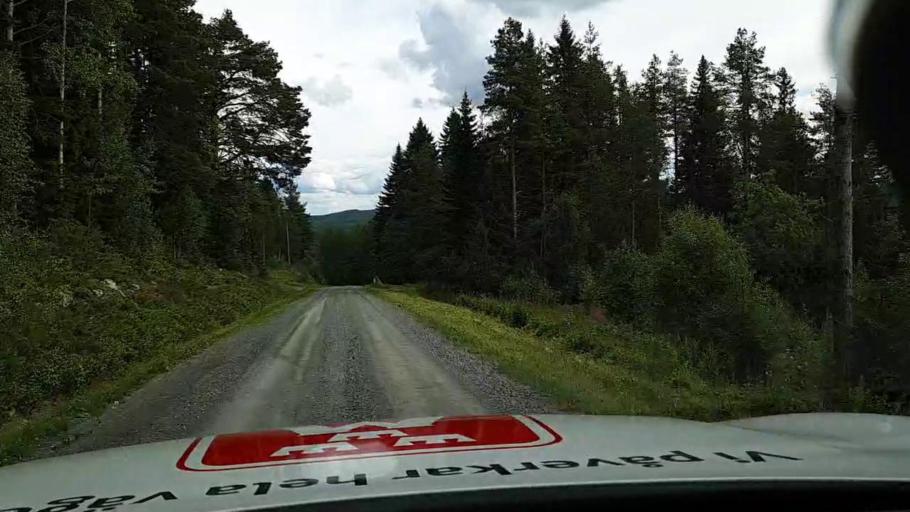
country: SE
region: Jaemtland
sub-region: Krokoms Kommun
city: Valla
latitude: 63.5829
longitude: 13.9760
